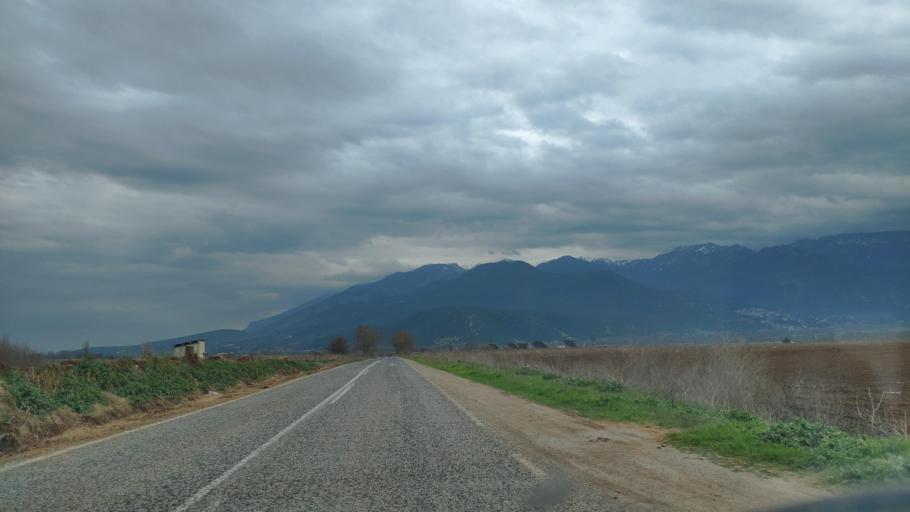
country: GR
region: Central Greece
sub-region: Nomos Fthiotidos
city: Amfikleia
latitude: 38.6923
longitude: 22.5284
